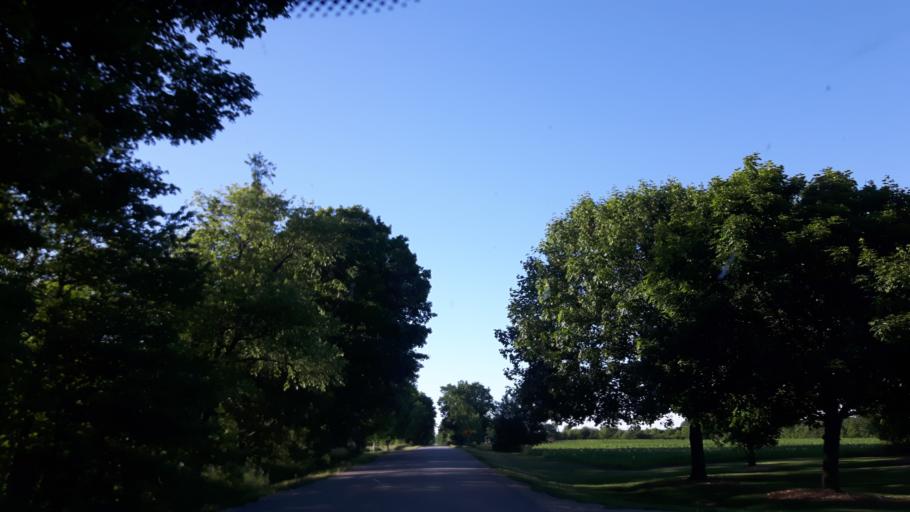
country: CA
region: Ontario
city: Goderich
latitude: 43.6389
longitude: -81.6643
